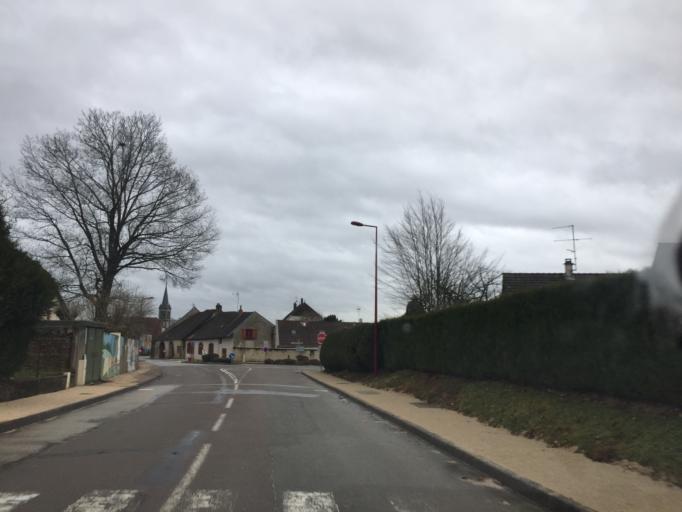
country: FR
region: Franche-Comte
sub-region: Departement du Jura
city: Dole
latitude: 47.1670
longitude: 5.5655
